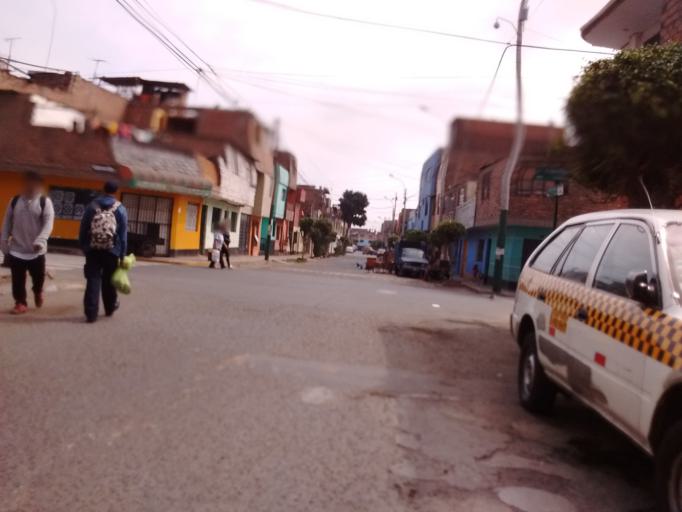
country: PE
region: Callao
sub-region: Callao
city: Callao
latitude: -12.0413
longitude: -77.0913
